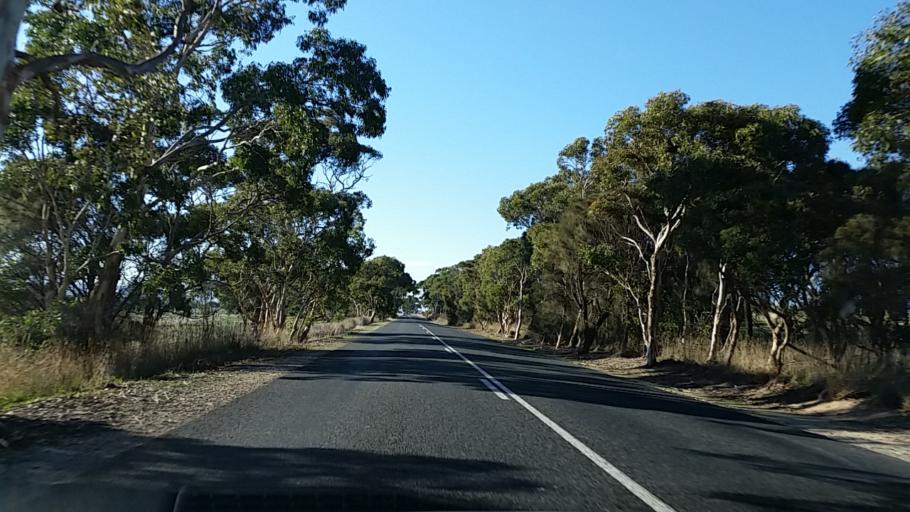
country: AU
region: South Australia
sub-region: Mount Barker
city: Macclesfield
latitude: -35.1561
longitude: 138.9354
